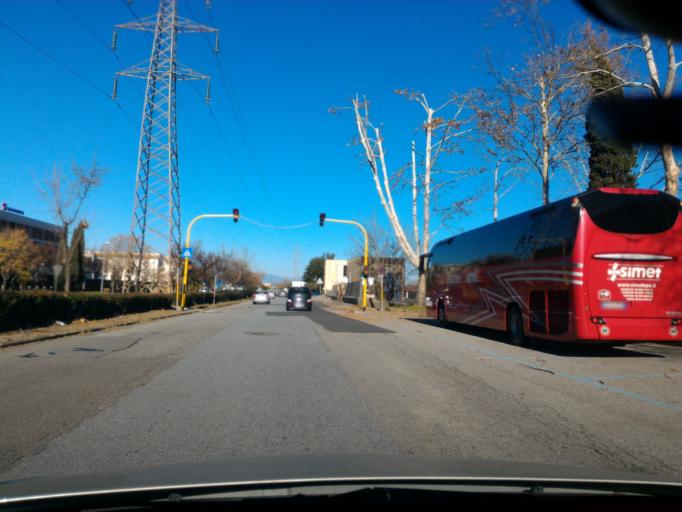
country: IT
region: Calabria
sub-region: Provincia di Cosenza
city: Cosenza
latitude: 39.3216
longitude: 16.2569
